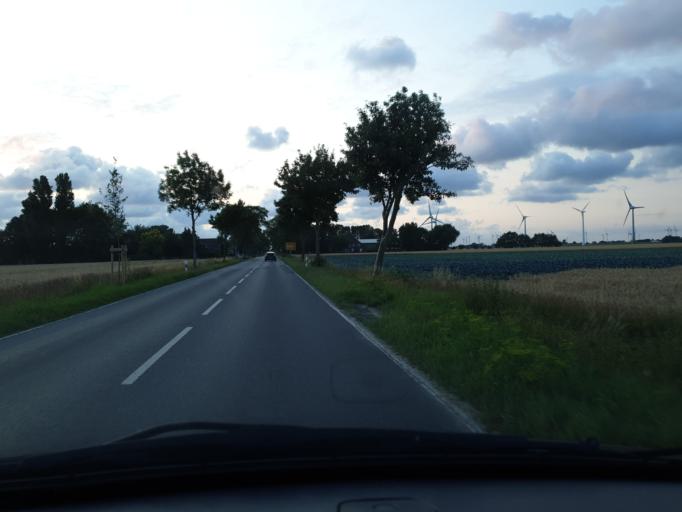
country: DE
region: Schleswig-Holstein
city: Kronprinzenkoog
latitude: 53.9714
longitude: 8.9253
